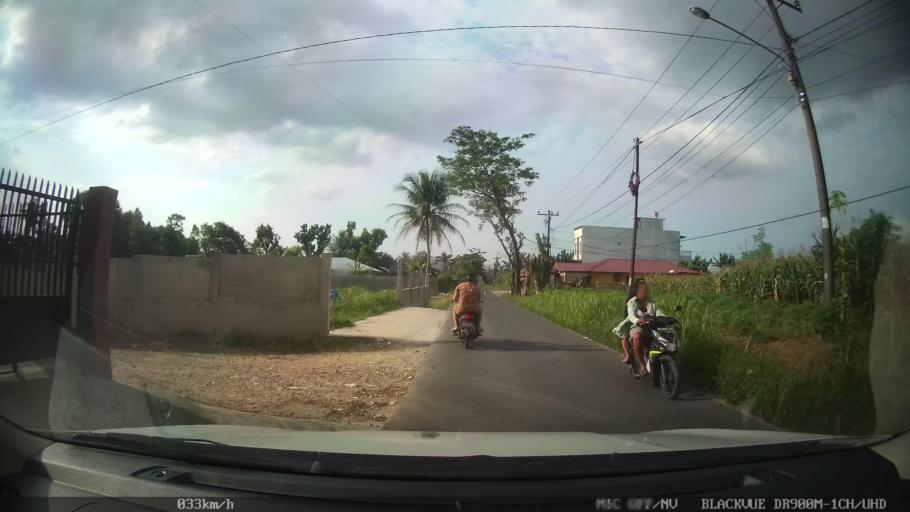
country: ID
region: North Sumatra
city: Sunggal
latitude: 3.5355
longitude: 98.6053
